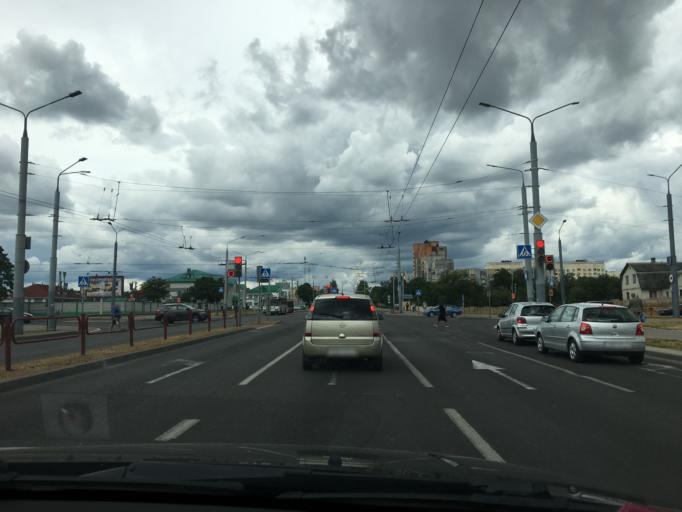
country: BY
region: Grodnenskaya
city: Hrodna
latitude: 53.7064
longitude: 23.8399
